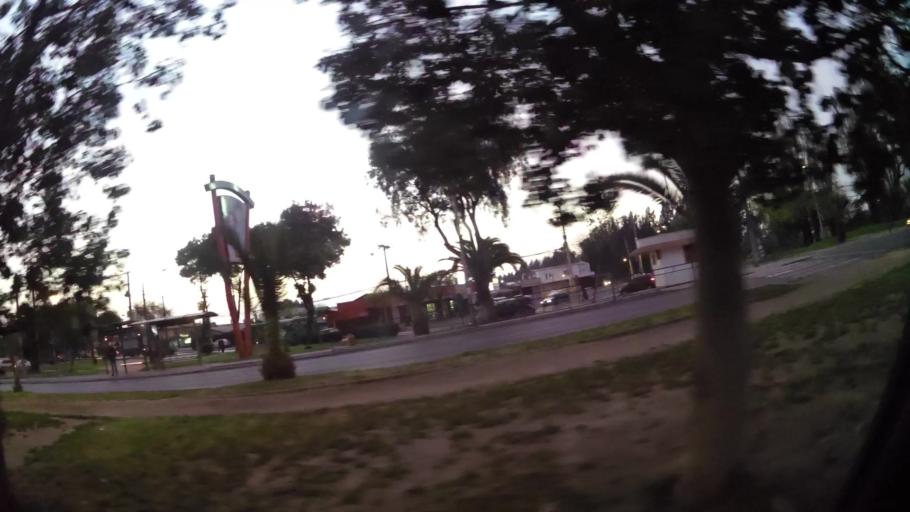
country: CL
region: Santiago Metropolitan
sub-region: Provincia de Santiago
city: Lo Prado
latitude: -33.4736
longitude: -70.7222
